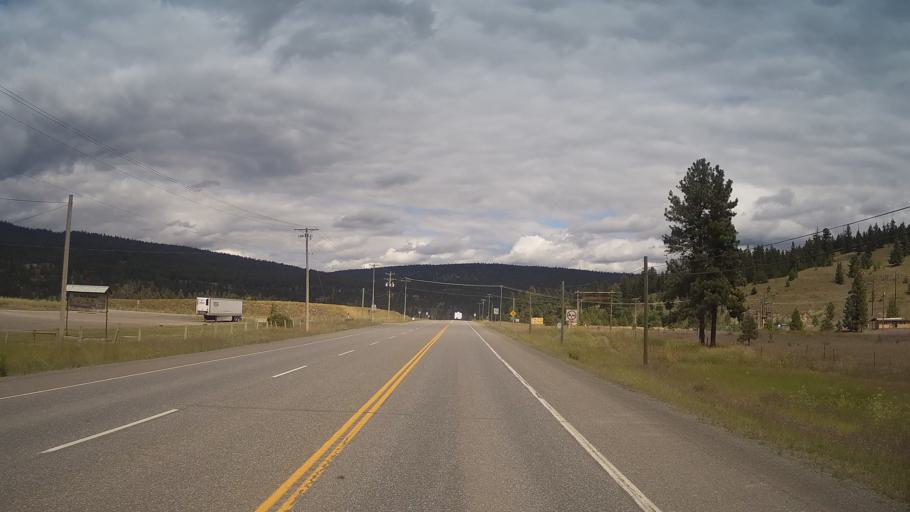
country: CA
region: British Columbia
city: Cache Creek
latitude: 51.0786
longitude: -121.5906
